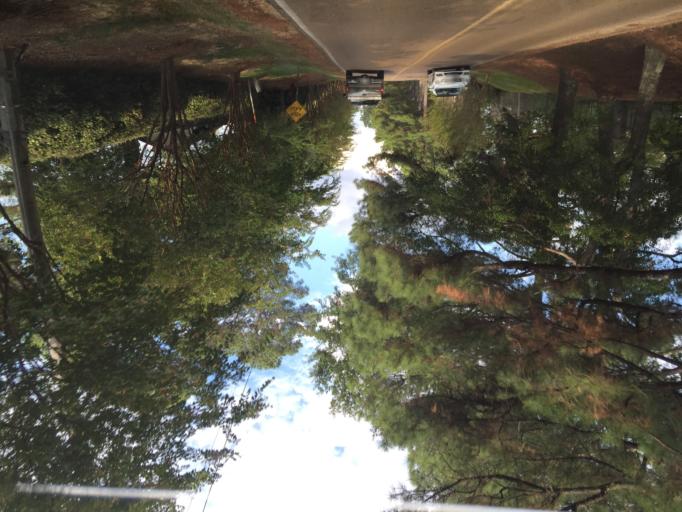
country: US
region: Mississippi
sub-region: Madison County
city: Madison
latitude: 32.4651
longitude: -90.0746
